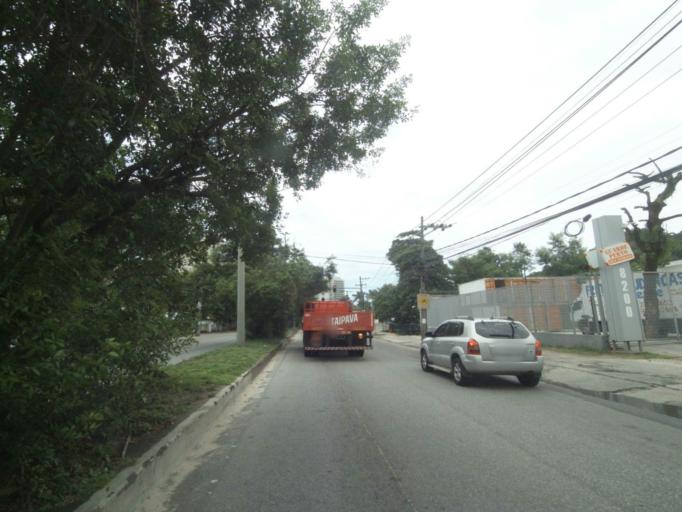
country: BR
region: Rio de Janeiro
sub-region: Nilopolis
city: Nilopolis
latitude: -22.9714
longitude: -43.4139
